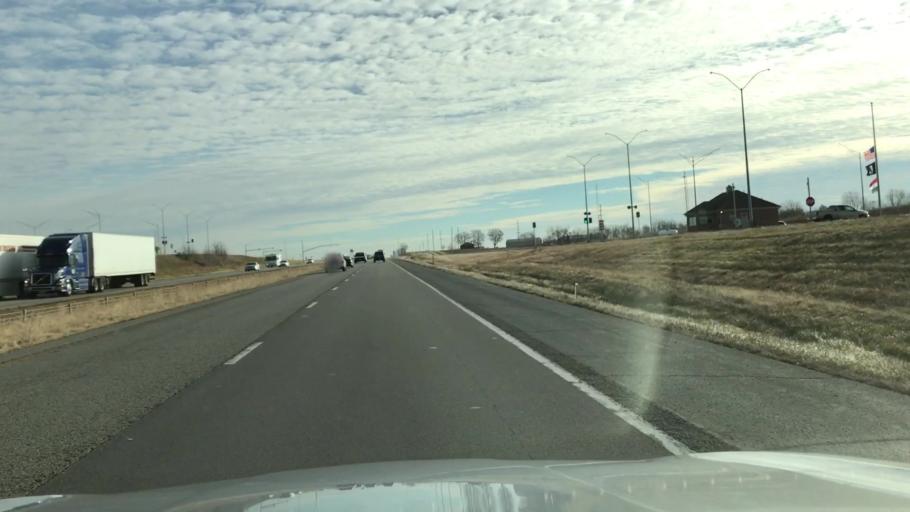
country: US
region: Missouri
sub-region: Lafayette County
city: Odessa
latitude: 39.0042
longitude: -93.8543
